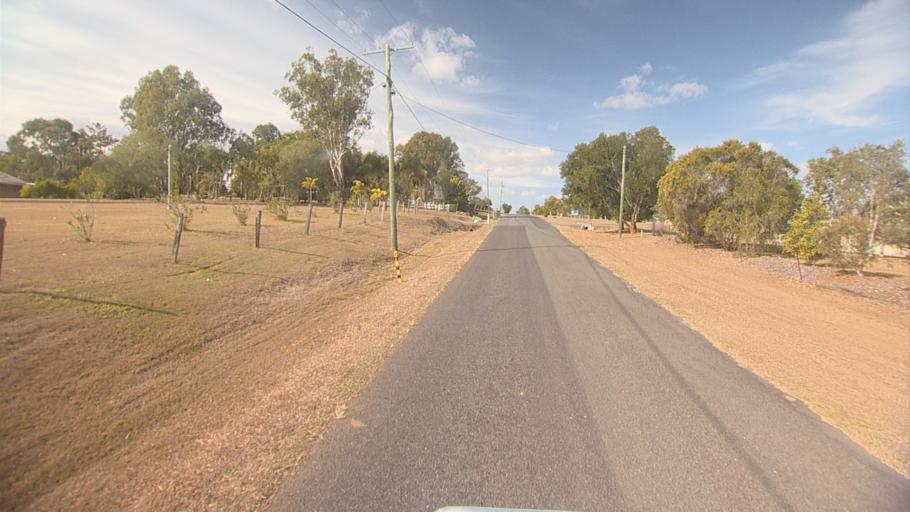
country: AU
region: Queensland
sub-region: Logan
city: Cedar Vale
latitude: -27.9153
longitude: 152.9918
